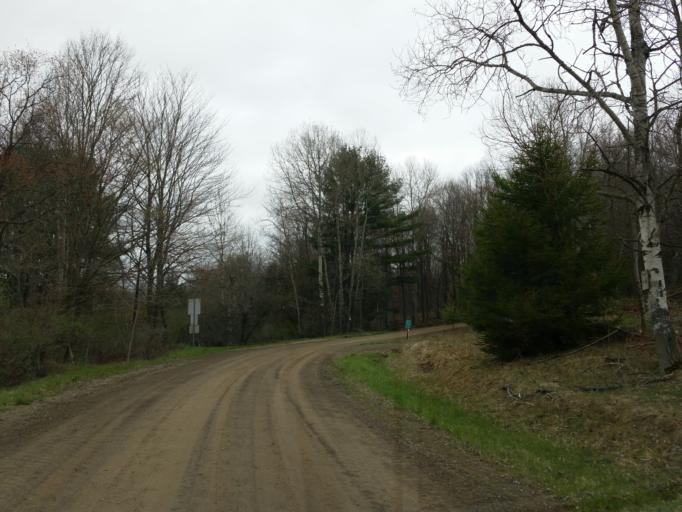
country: US
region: New York
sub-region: Allegany County
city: Andover
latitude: 42.0449
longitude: -77.7485
